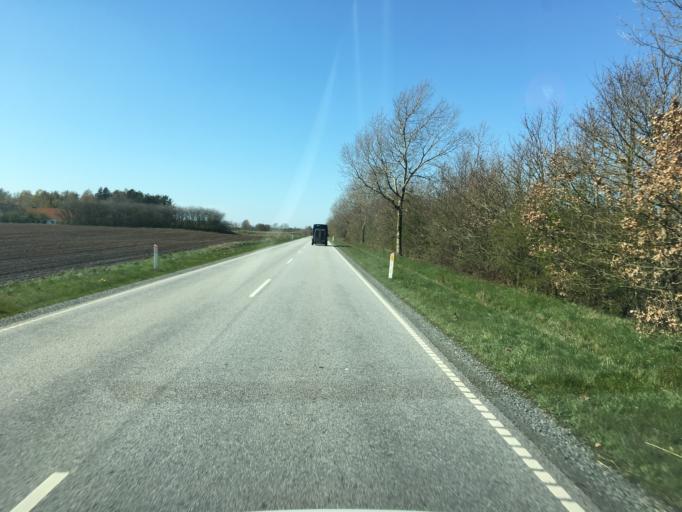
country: DK
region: South Denmark
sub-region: Aabenraa Kommune
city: Tinglev
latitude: 54.9535
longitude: 9.3405
